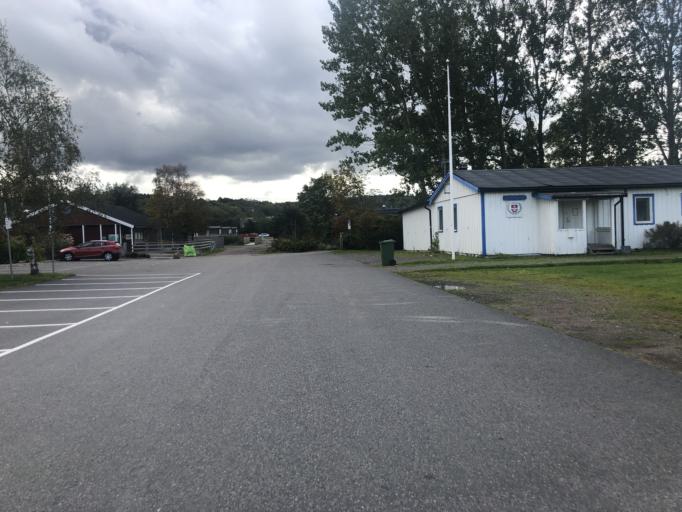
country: SE
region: Vaestra Goetaland
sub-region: Molndal
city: Moelndal
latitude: 57.6467
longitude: 11.9937
